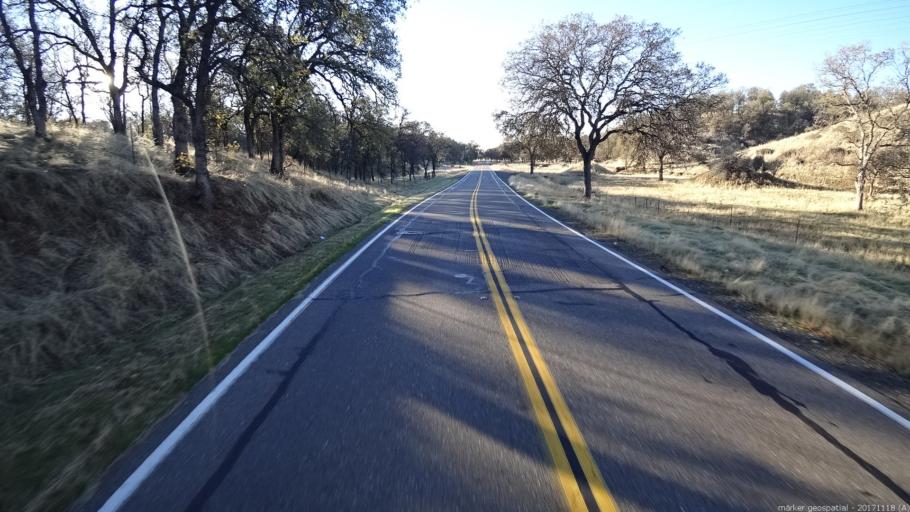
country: US
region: California
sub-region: Shasta County
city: Cottonwood
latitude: 40.4124
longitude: -122.2824
